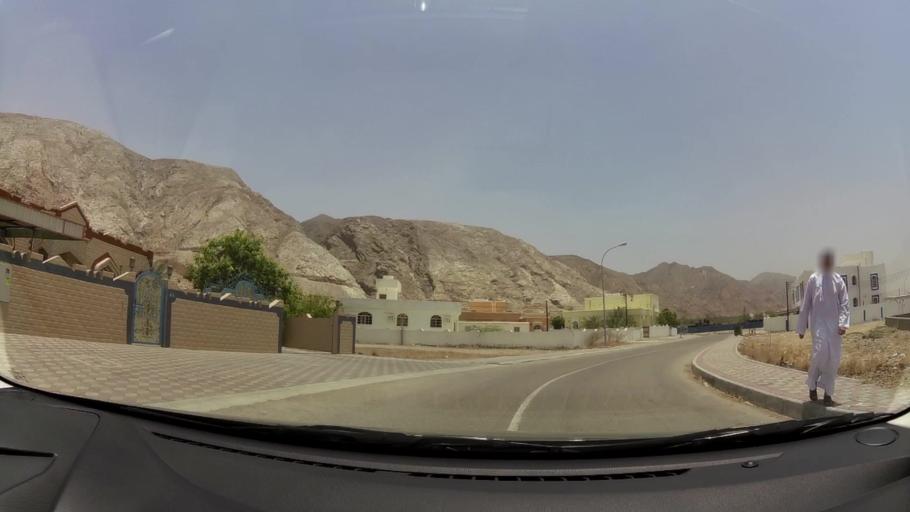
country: OM
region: Muhafazat Masqat
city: Bawshar
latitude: 23.5513
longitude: 58.4108
